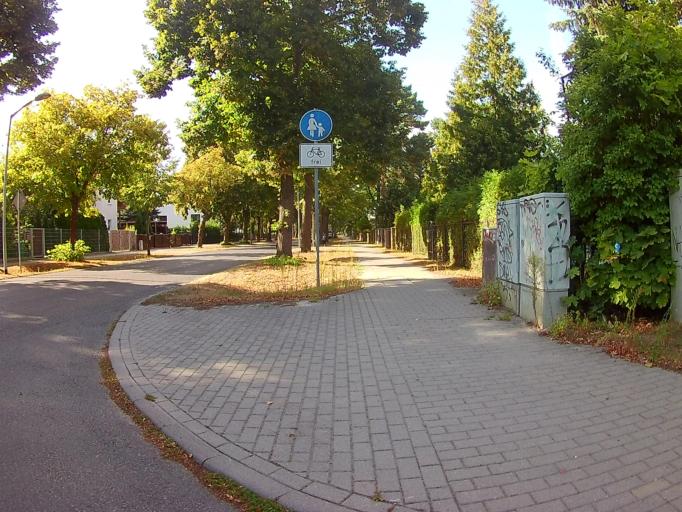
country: DE
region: Brandenburg
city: Zeuthen
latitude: 52.3748
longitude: 13.6008
